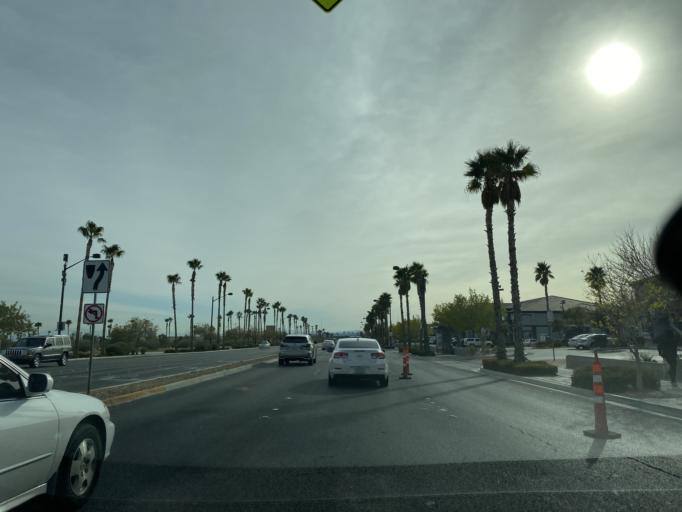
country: US
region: Nevada
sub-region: Clark County
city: Summerlin South
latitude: 36.2881
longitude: -115.2879
